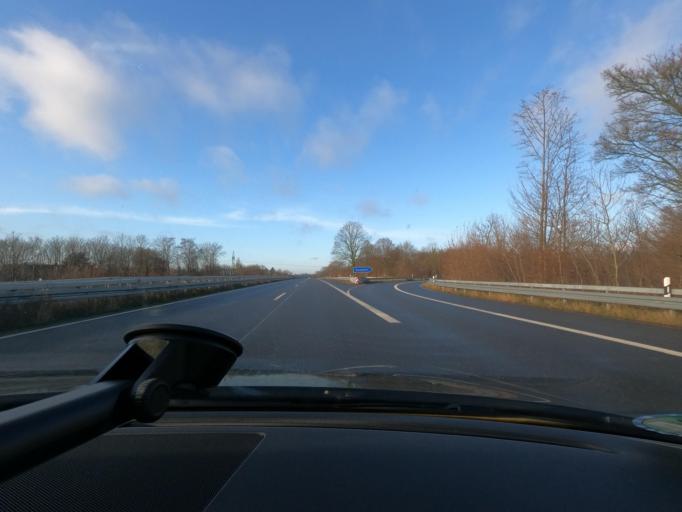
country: DE
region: North Rhine-Westphalia
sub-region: Regierungsbezirk Dusseldorf
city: Ratingen
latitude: 51.3499
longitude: 6.8249
